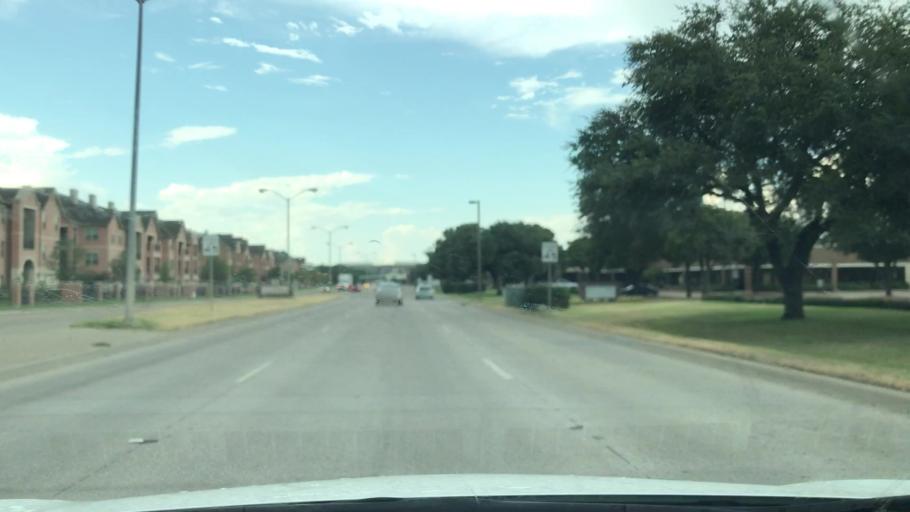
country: US
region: Texas
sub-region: Dallas County
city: Farmers Branch
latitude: 32.8962
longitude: -96.9185
